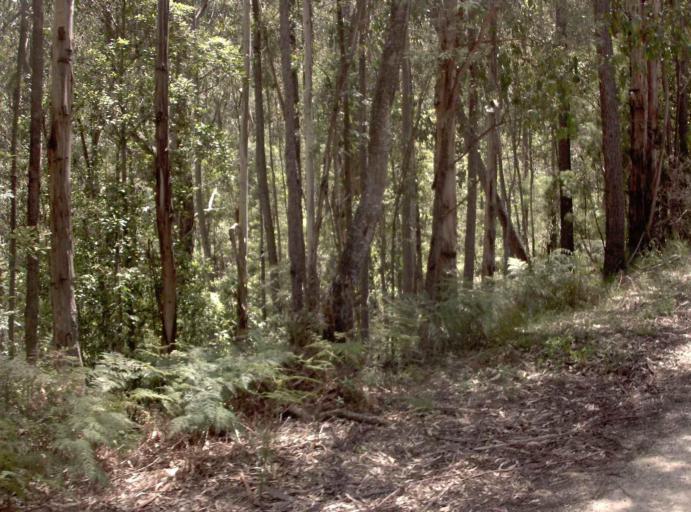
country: AU
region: New South Wales
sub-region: Bombala
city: Bombala
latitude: -37.5783
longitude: 148.9393
